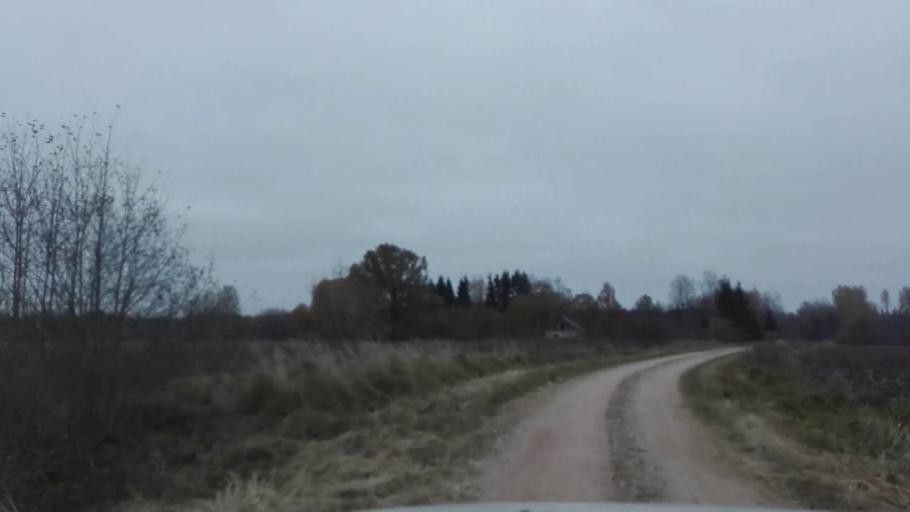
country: EE
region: Jogevamaa
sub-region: Poltsamaa linn
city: Poltsamaa
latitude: 58.4365
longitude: 25.9652
